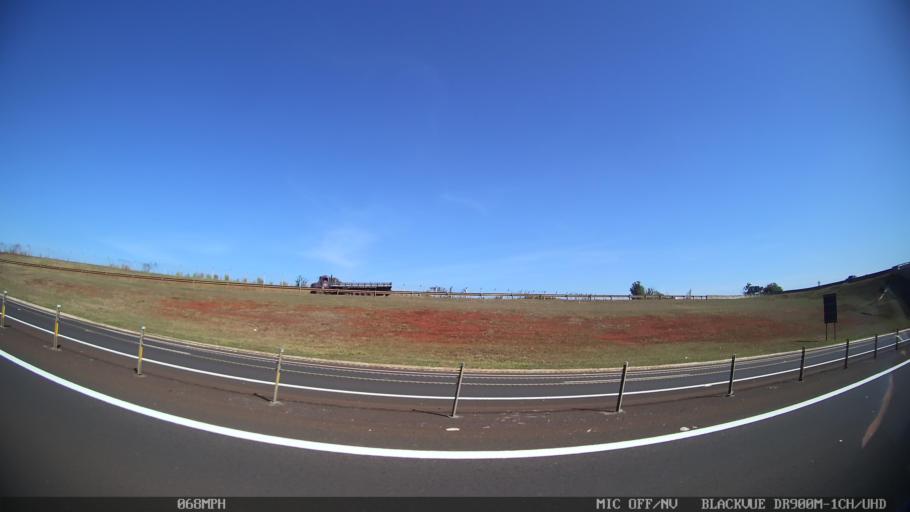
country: BR
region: Sao Paulo
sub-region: Ribeirao Preto
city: Ribeirao Preto
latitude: -21.1982
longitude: -47.8765
